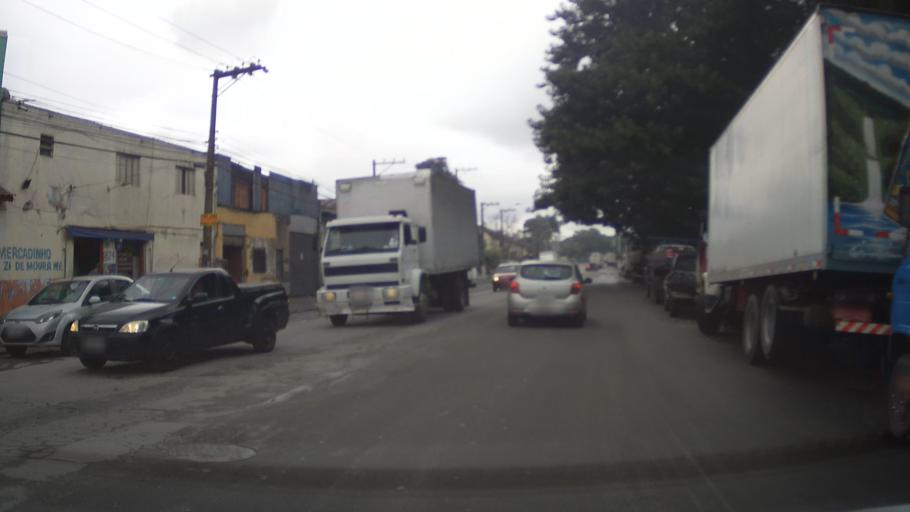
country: BR
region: Sao Paulo
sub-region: Guarulhos
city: Guarulhos
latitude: -23.4644
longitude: -46.4784
